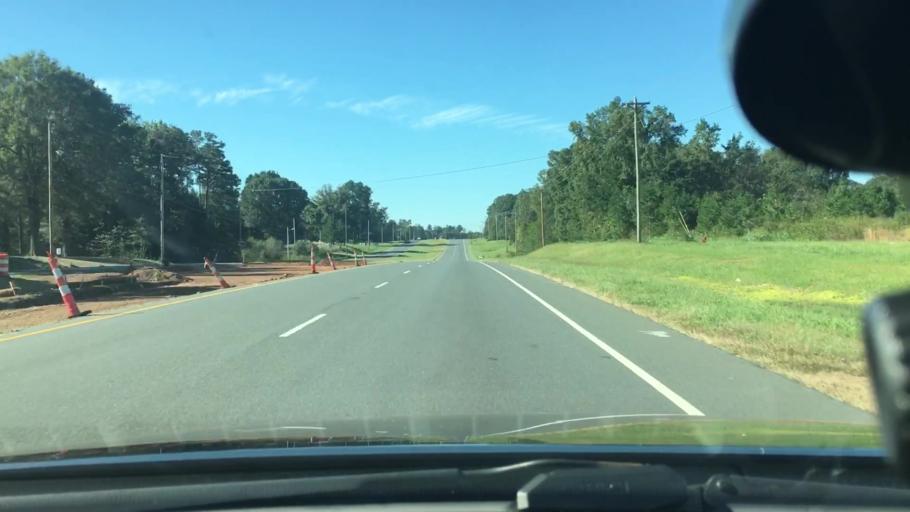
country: US
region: North Carolina
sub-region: Stanly County
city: Albemarle
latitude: 35.3224
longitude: -80.2473
